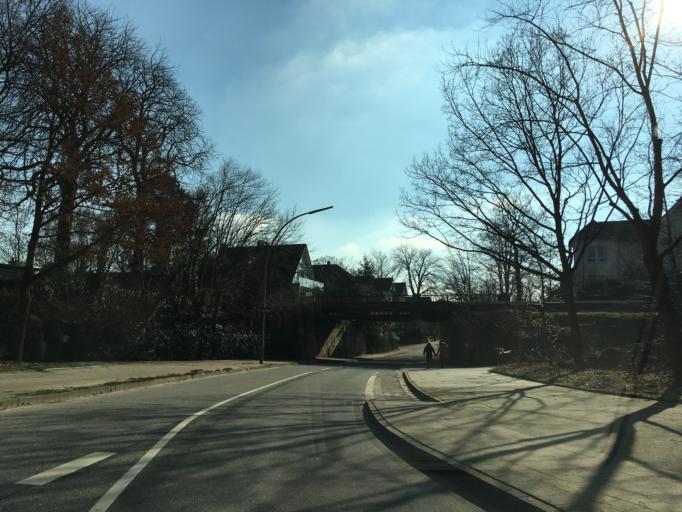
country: DE
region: Hamburg
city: Eidelstedt
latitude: 53.5589
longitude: 9.8645
